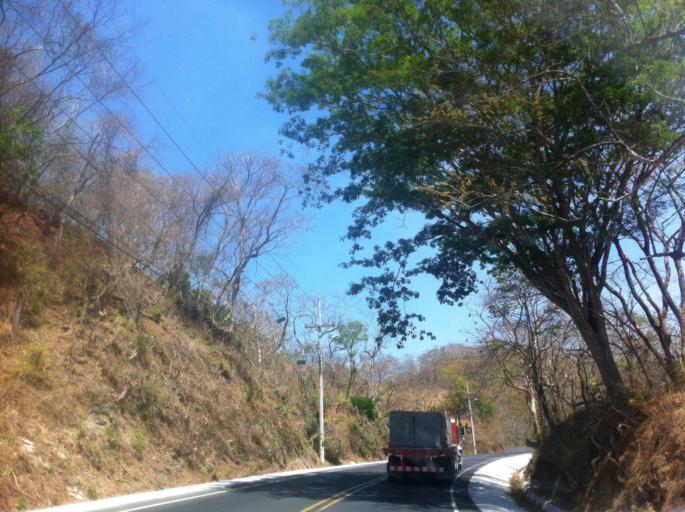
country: CR
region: Guanacaste
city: Santa Cruz
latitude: 10.2156
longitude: -85.5132
